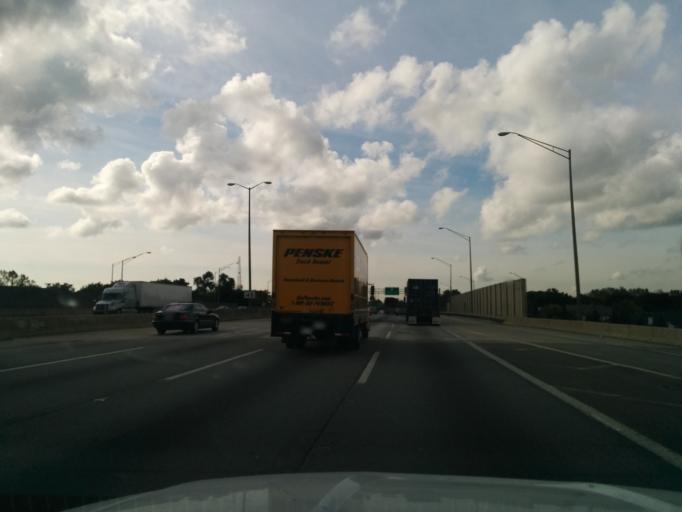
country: US
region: Illinois
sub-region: Cook County
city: Hillside
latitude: 41.8627
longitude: -87.9185
